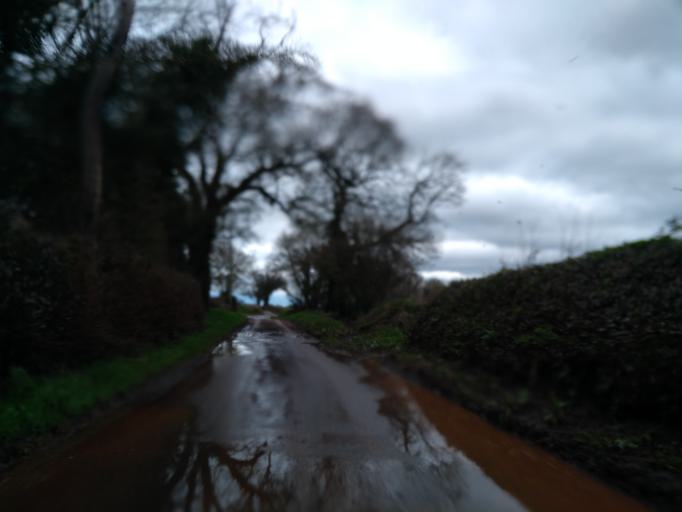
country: GB
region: England
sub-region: Devon
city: Exeter
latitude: 50.7895
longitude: -3.5683
